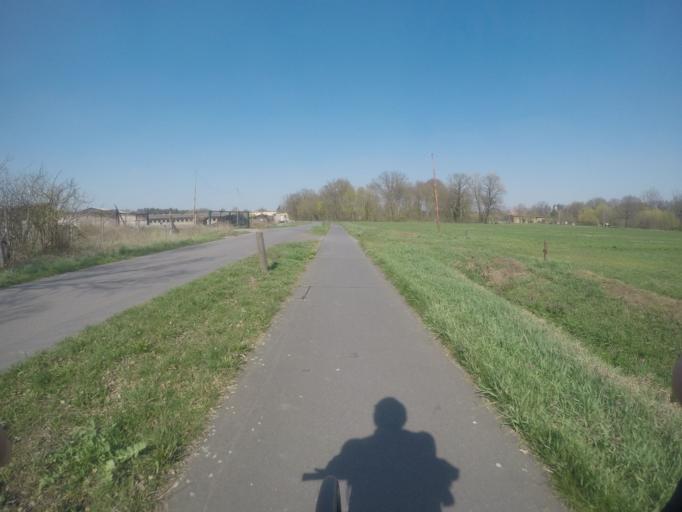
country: DE
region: Brandenburg
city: Falkensee
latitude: 52.6353
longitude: 13.0860
